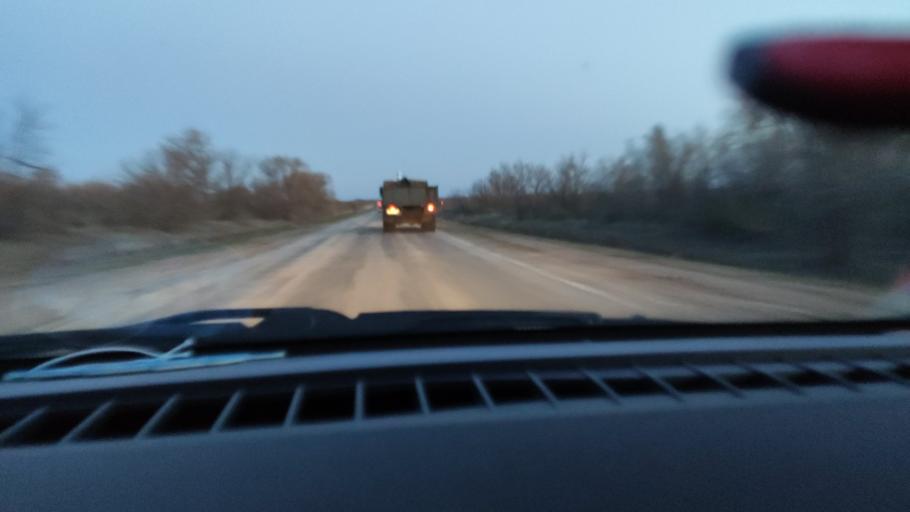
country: RU
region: Saratov
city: Rovnoye
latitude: 51.0119
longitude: 46.0978
